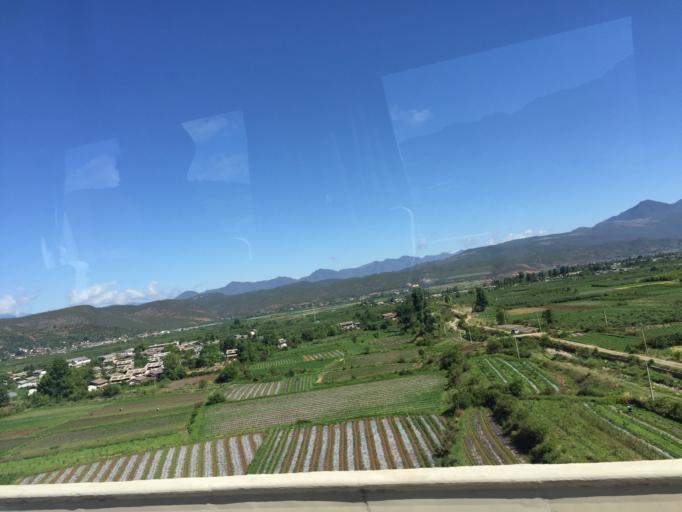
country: CN
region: Yunnan
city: Huangshan
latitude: 26.8238
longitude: 100.1230
